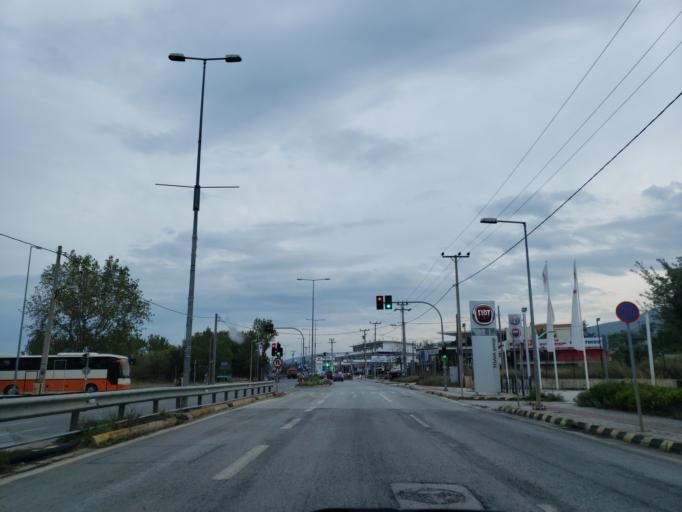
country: GR
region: Attica
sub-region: Nomarchia Anatolikis Attikis
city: Aghios Panteleimon
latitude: 38.1046
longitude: 23.9698
